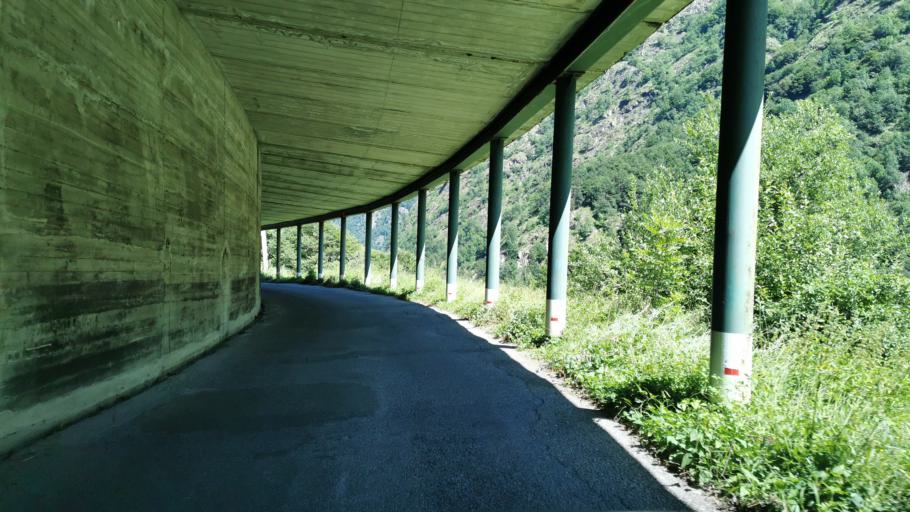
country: IT
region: Piedmont
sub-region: Provincia di Cuneo
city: Entracque
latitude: 44.1998
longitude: 7.3645
